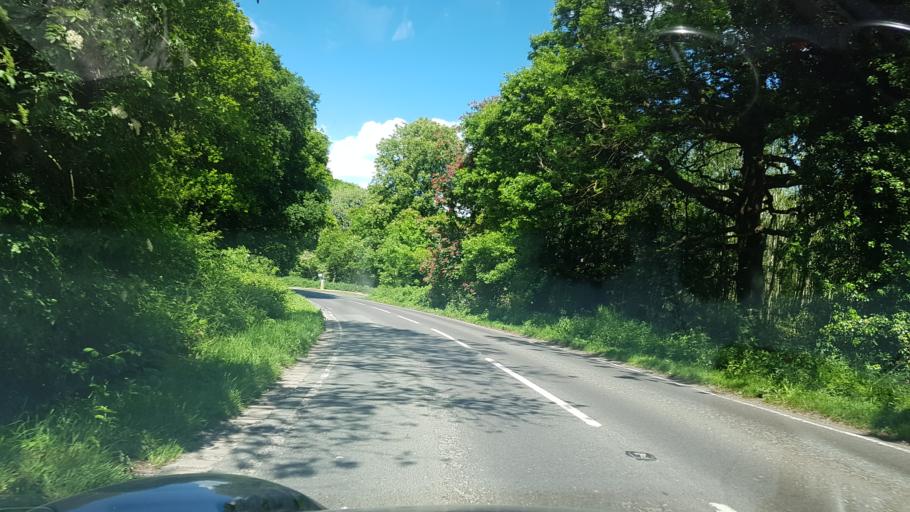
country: GB
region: England
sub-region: Surrey
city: Cranleigh
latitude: 51.1364
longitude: -0.5327
